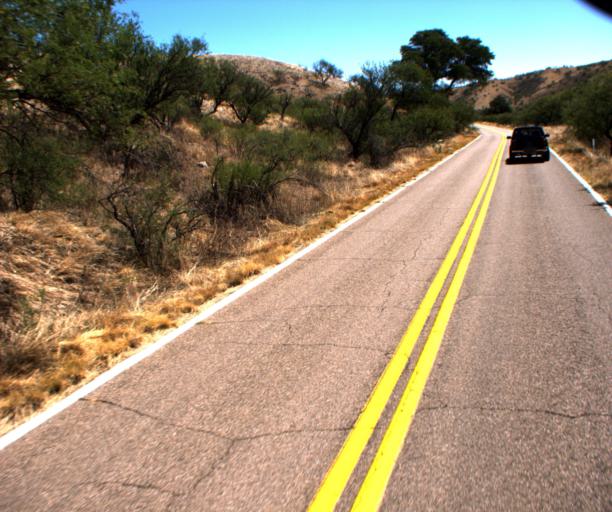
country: US
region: Arizona
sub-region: Santa Cruz County
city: Rio Rico
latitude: 31.3965
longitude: -111.0366
